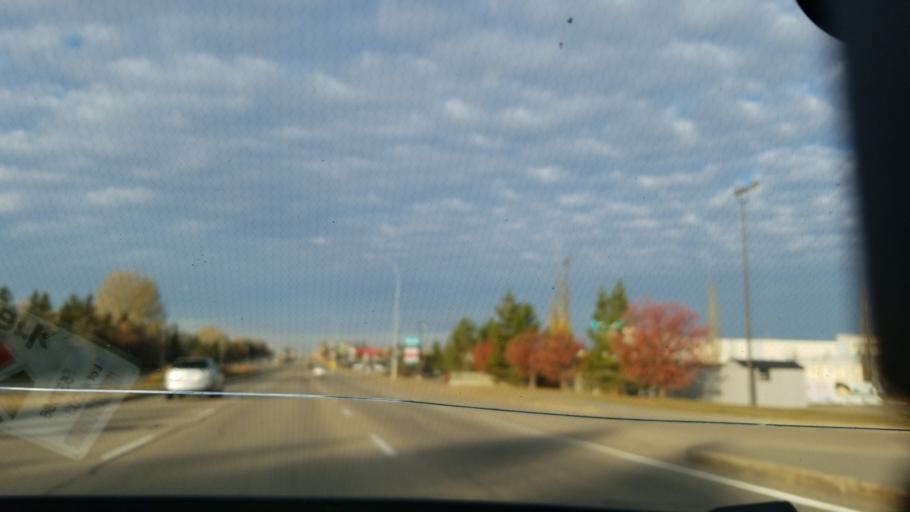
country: CA
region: Alberta
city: Sherwood Park
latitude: 53.5413
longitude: -113.3051
